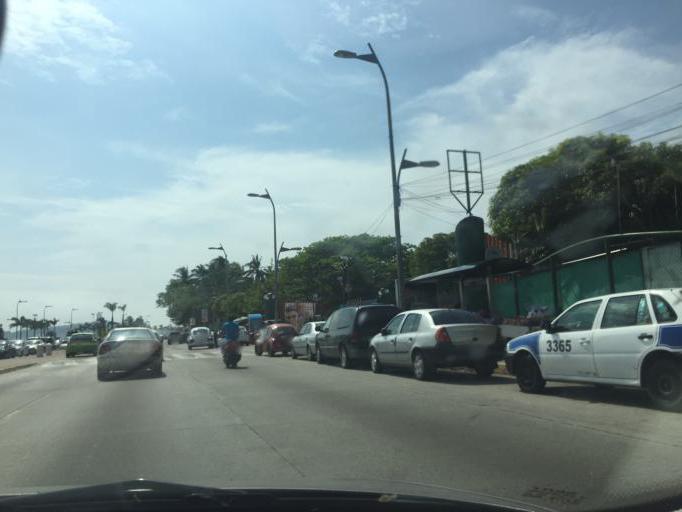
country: MX
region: Guerrero
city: Acapulco de Juarez
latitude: 16.8593
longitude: -99.8867
